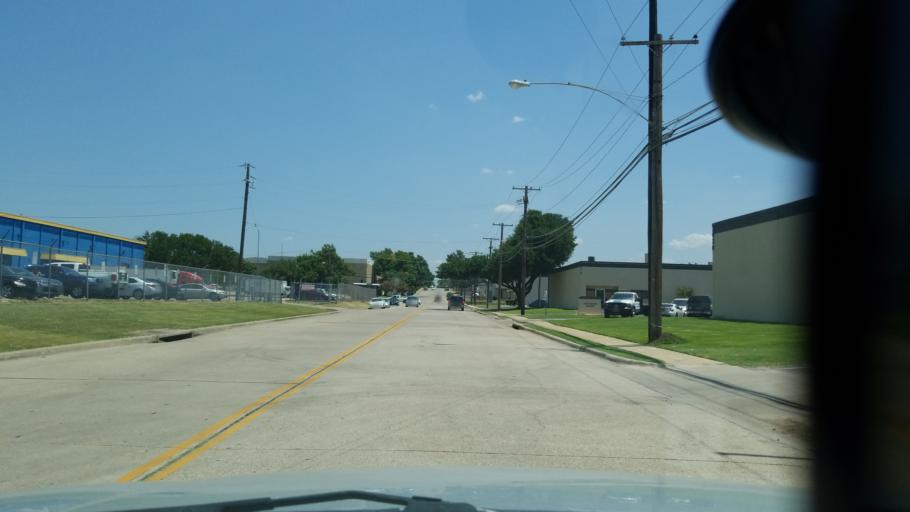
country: US
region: Texas
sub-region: Dallas County
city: Farmers Branch
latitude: 32.9038
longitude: -96.8885
